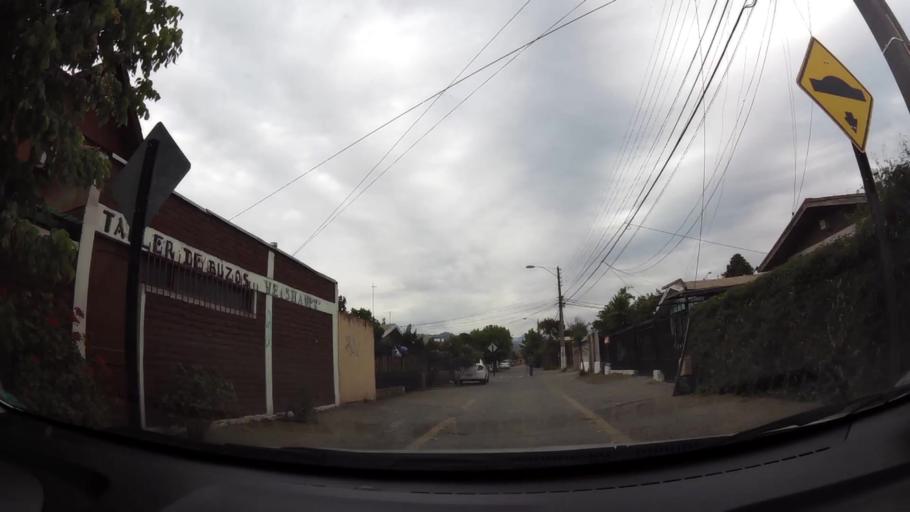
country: CL
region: O'Higgins
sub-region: Provincia de Cachapoal
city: Rancagua
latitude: -34.1597
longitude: -70.7312
